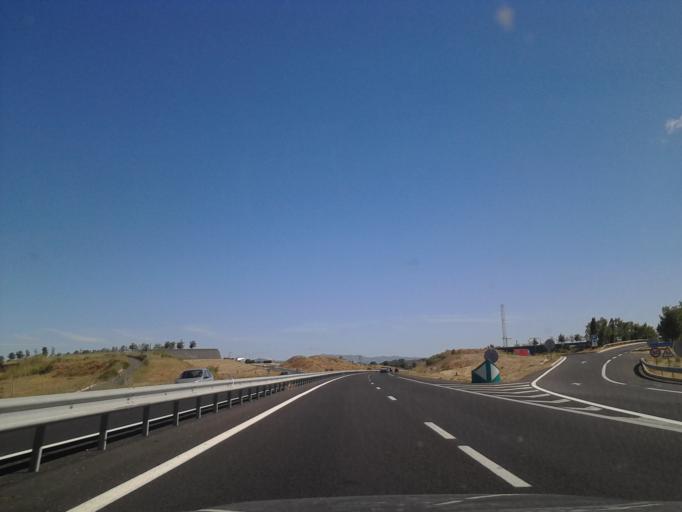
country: FR
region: Languedoc-Roussillon
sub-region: Departement de l'Herault
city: Paulhan
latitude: 43.5393
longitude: 3.4442
